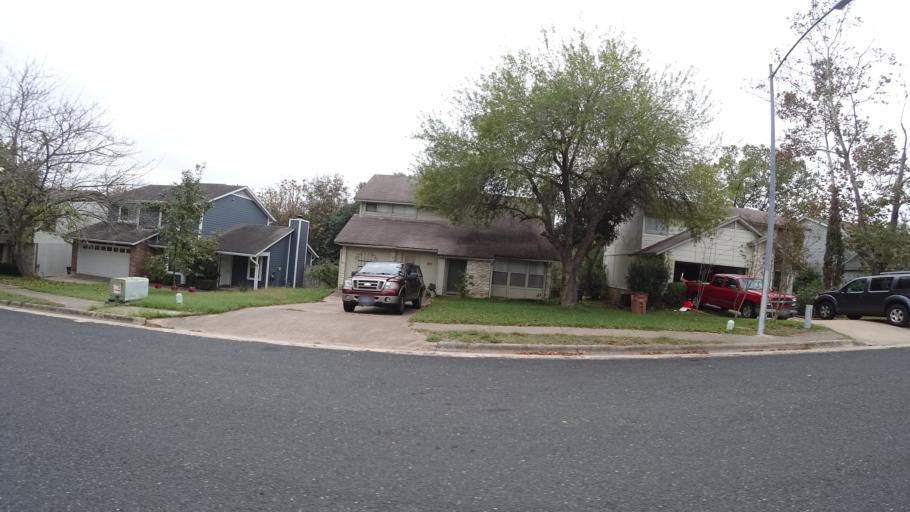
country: US
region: Texas
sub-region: Travis County
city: Barton Creek
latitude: 30.2396
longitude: -97.8975
